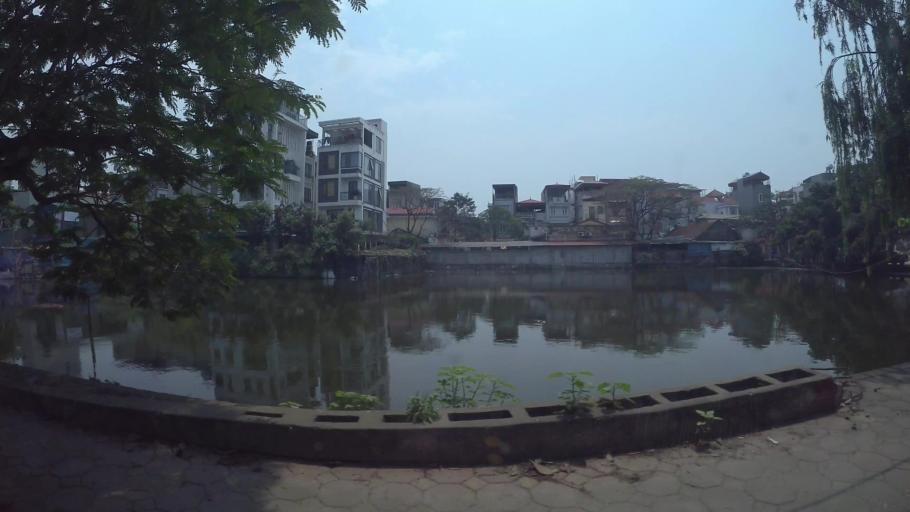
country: VN
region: Ha Noi
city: Van Dien
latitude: 20.9565
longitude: 105.8290
